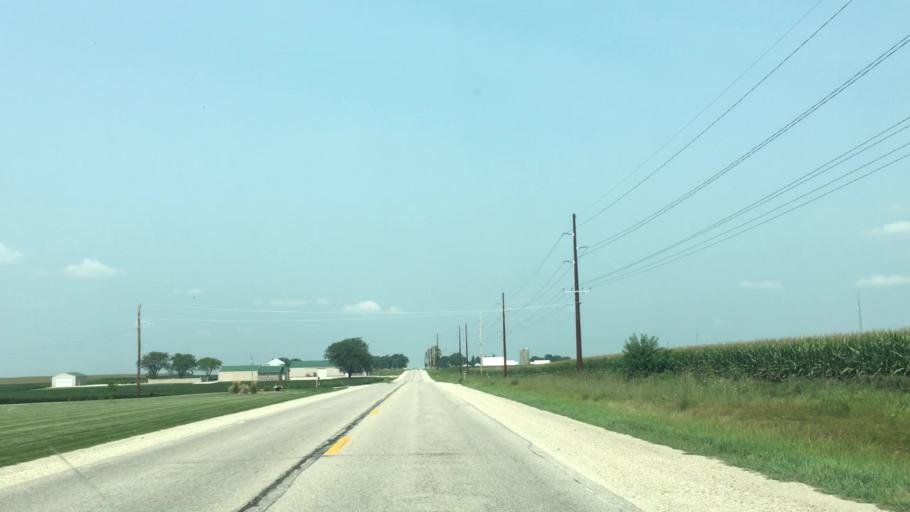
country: US
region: Iowa
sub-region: Buchanan County
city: Independence
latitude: 42.4330
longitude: -91.8898
